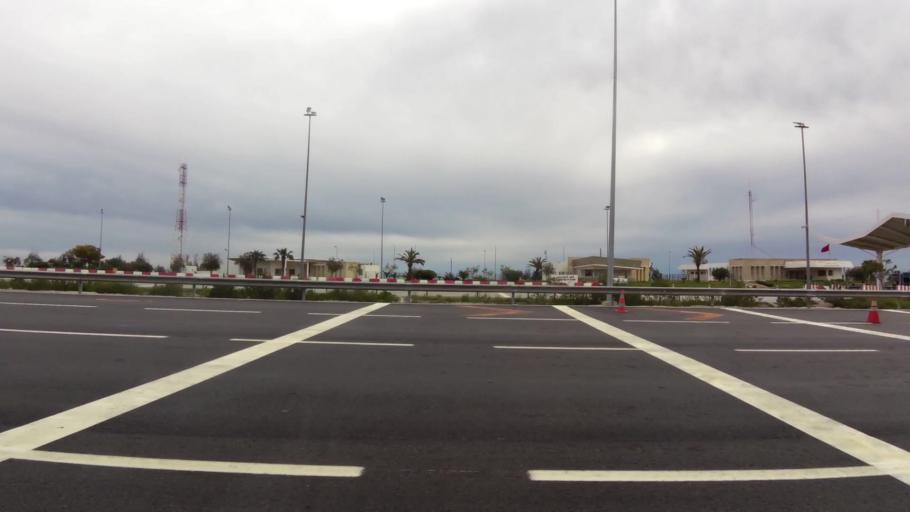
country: ES
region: Ceuta
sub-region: Ceuta
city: Ceuta
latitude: 35.7446
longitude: -5.3541
